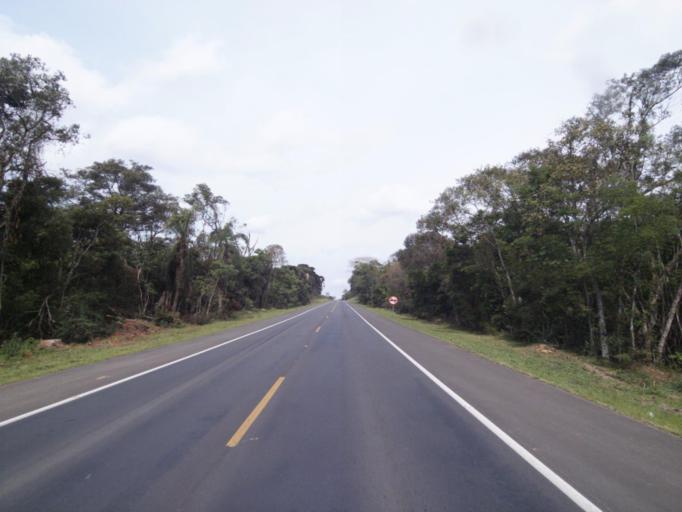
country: BR
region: Parana
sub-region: Irati
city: Irati
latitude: -25.4696
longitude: -50.5026
